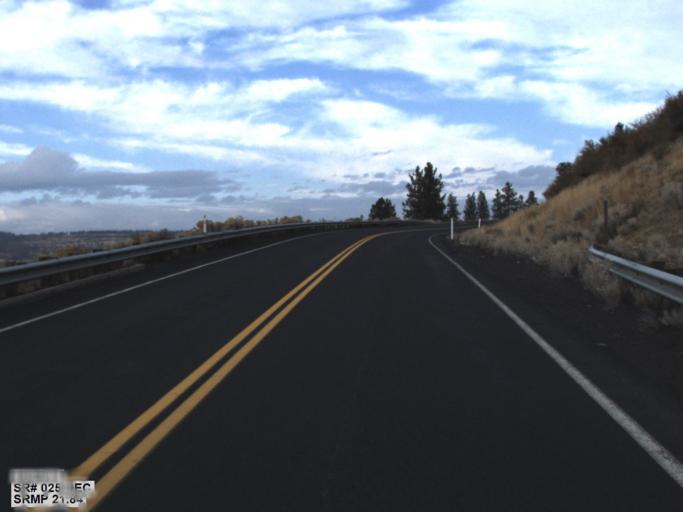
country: US
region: Washington
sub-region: Lincoln County
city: Davenport
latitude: 47.9067
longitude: -118.2896
